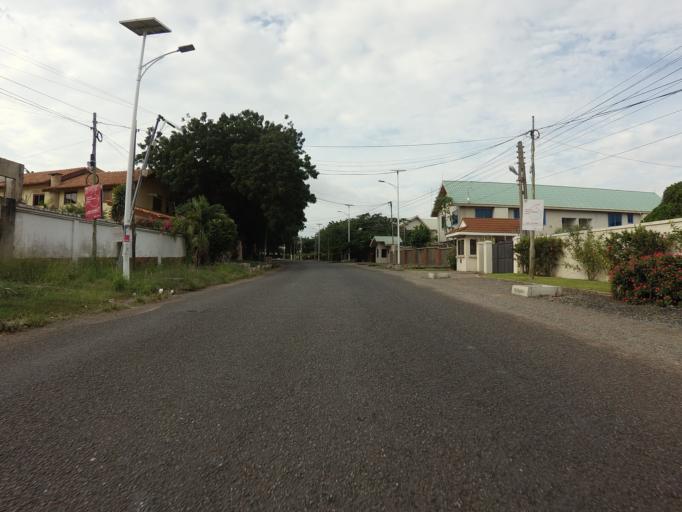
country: GH
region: Greater Accra
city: Accra
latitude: 5.5842
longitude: -0.1692
